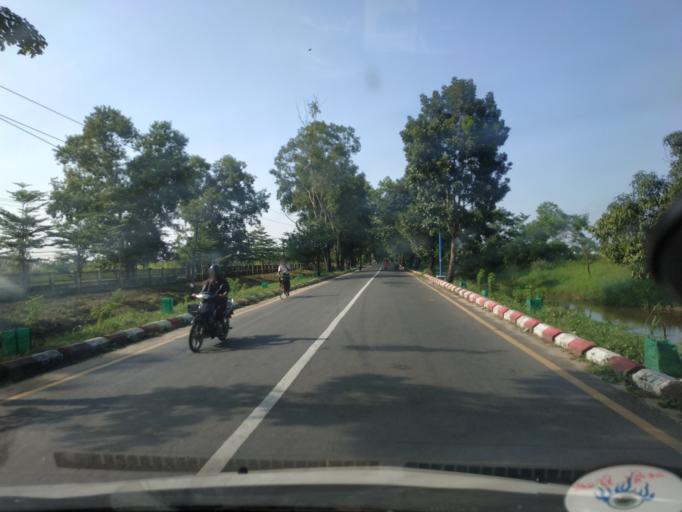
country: MM
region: Ayeyarwady
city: Pathein
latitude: 16.8049
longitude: 94.7583
